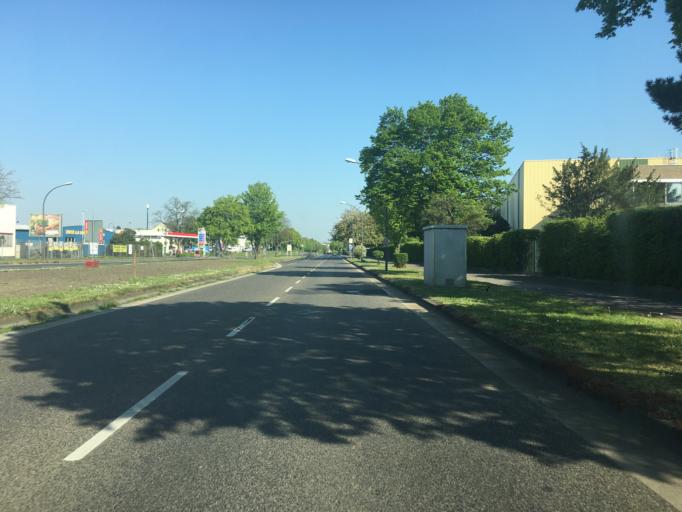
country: DE
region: North Rhine-Westphalia
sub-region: Regierungsbezirk Koln
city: Muelheim
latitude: 50.9778
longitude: 7.0039
